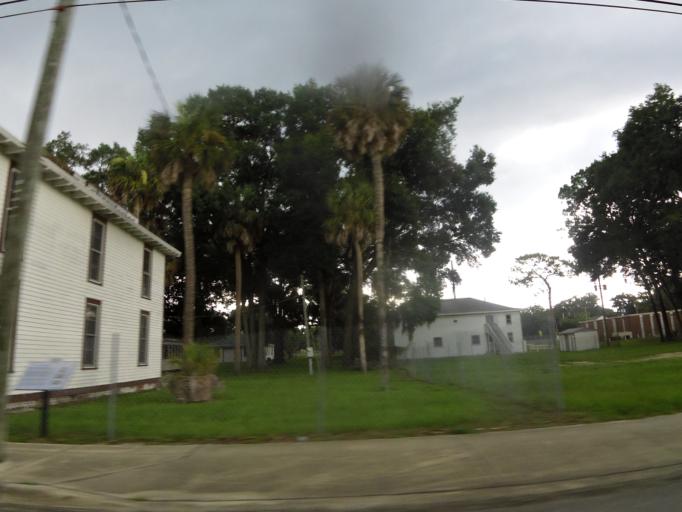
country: US
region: Florida
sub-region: Duval County
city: Jacksonville
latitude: 30.3337
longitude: -81.5934
